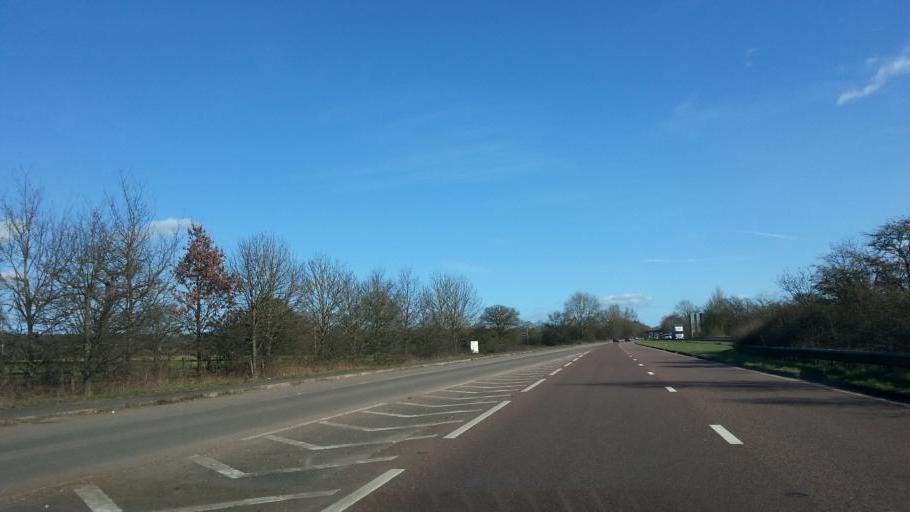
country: GB
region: England
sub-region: Solihull
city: Meriden
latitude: 52.4429
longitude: -1.6489
